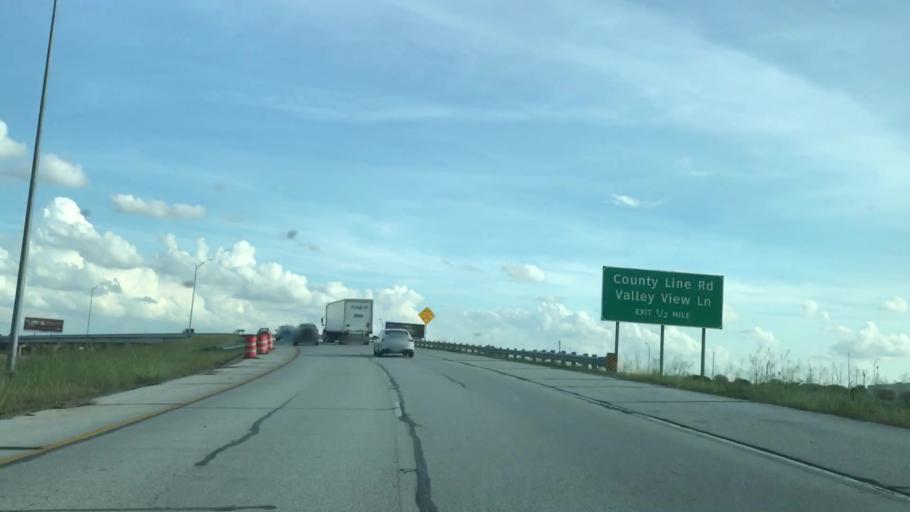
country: US
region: Texas
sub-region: Tarrant County
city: Euless
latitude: 32.8385
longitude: -97.0418
